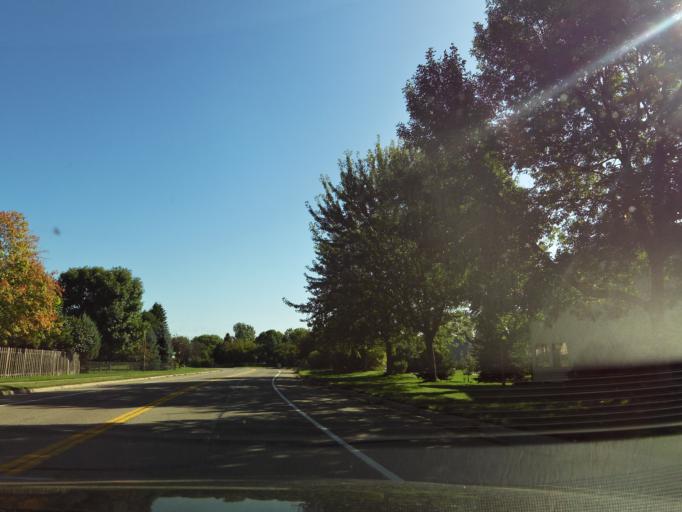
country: US
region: Minnesota
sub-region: Scott County
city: Savage
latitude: 44.7370
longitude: -93.3428
